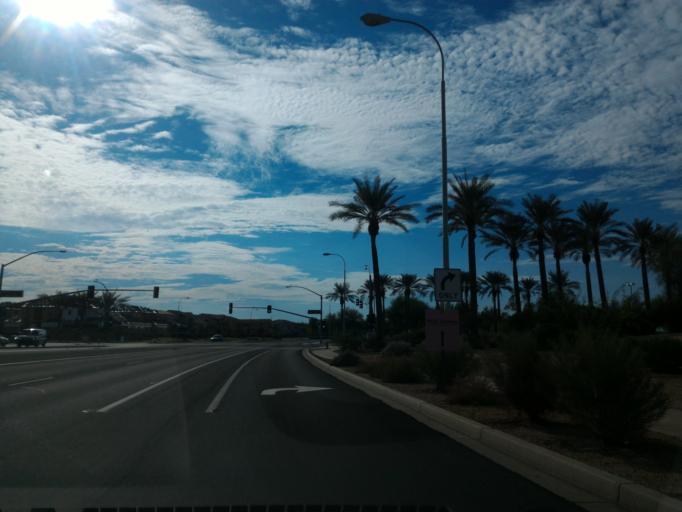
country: US
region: Arizona
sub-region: Maricopa County
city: Sun Lakes
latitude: 33.2442
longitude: -111.8780
